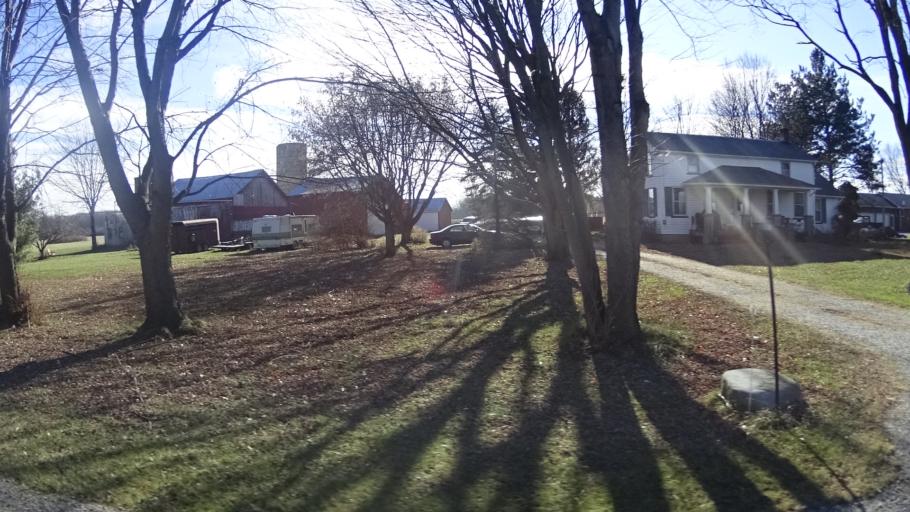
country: US
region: Ohio
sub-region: Lorain County
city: South Amherst
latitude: 41.3459
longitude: -82.2813
